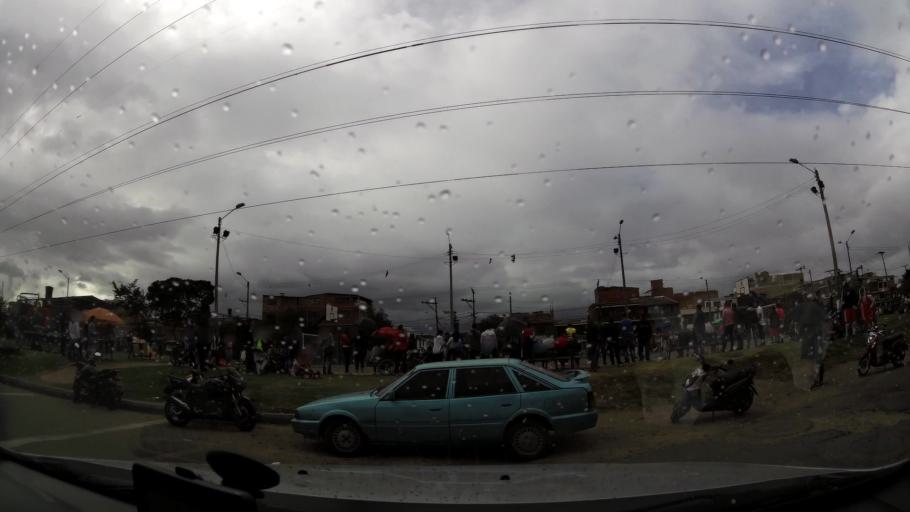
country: CO
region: Bogota D.C.
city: Bogota
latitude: 4.6068
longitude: -74.1378
